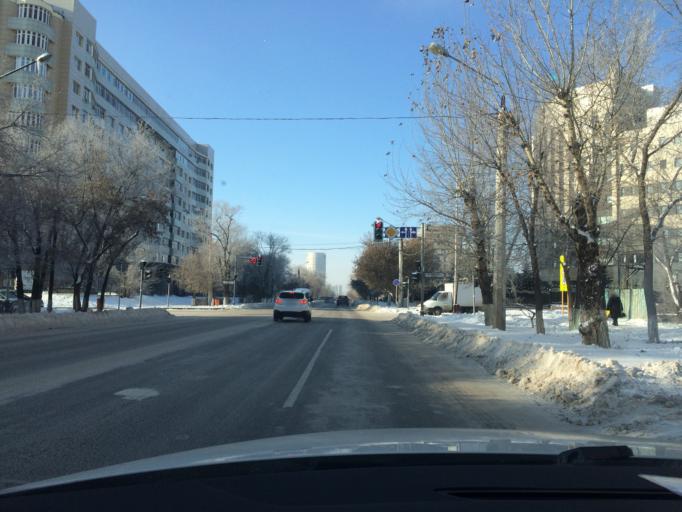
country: KZ
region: Astana Qalasy
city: Astana
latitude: 51.1721
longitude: 71.4315
